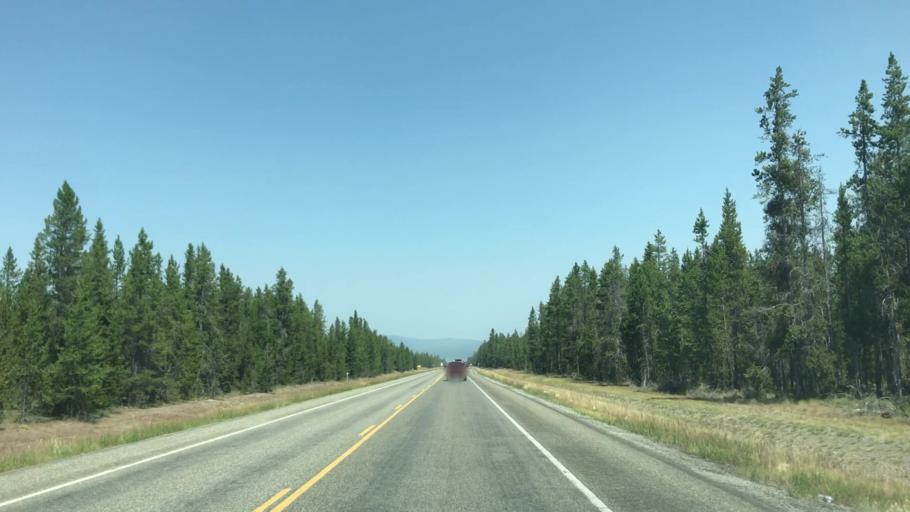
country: US
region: Montana
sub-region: Gallatin County
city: West Yellowstone
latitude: 44.6819
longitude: -111.1008
